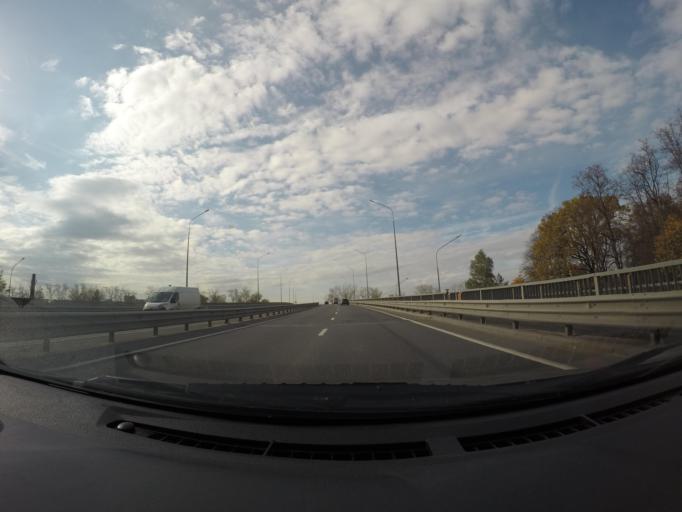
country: RU
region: Moscow
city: Severnyy
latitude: 55.9236
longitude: 37.5312
